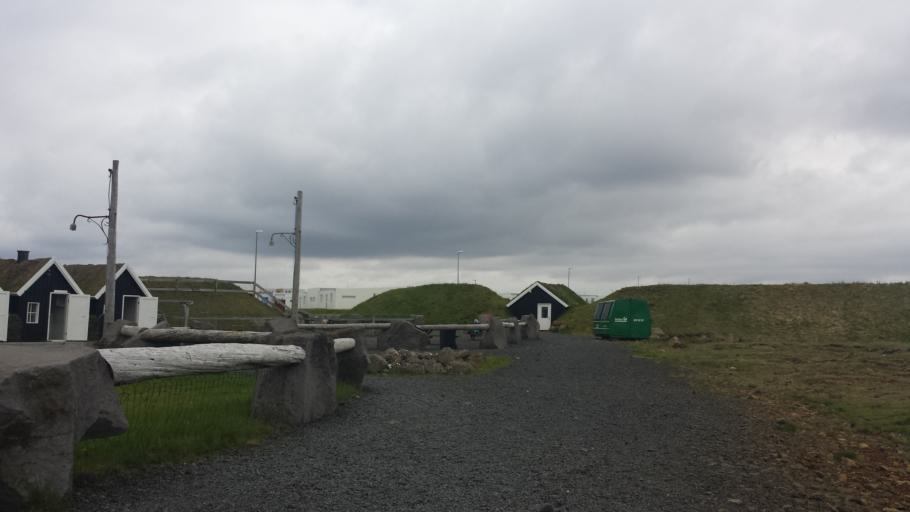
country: IS
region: Southern Peninsula
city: Reykjanesbaer
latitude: 63.9750
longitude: -22.5274
